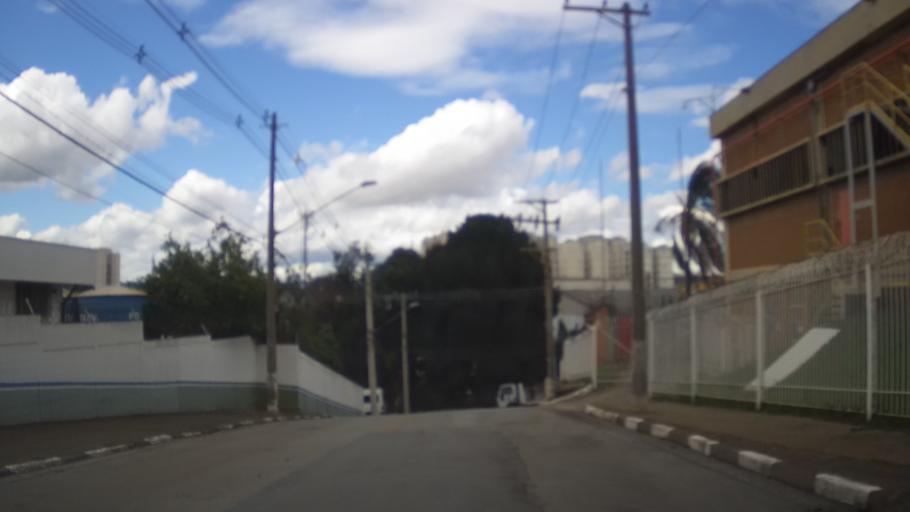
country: BR
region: Sao Paulo
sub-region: Guarulhos
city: Guarulhos
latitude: -23.4919
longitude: -46.5561
